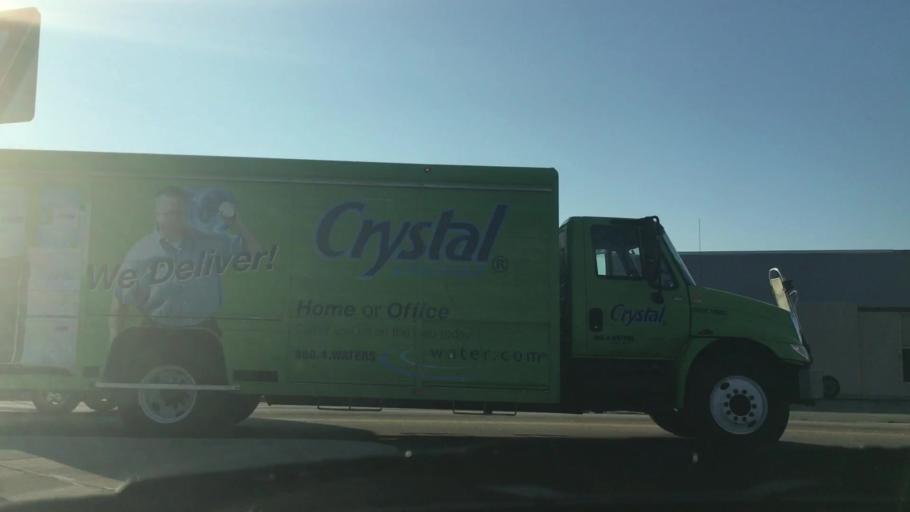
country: US
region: Virginia
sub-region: City of Norfolk
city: Norfolk
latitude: 36.8902
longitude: -76.2384
